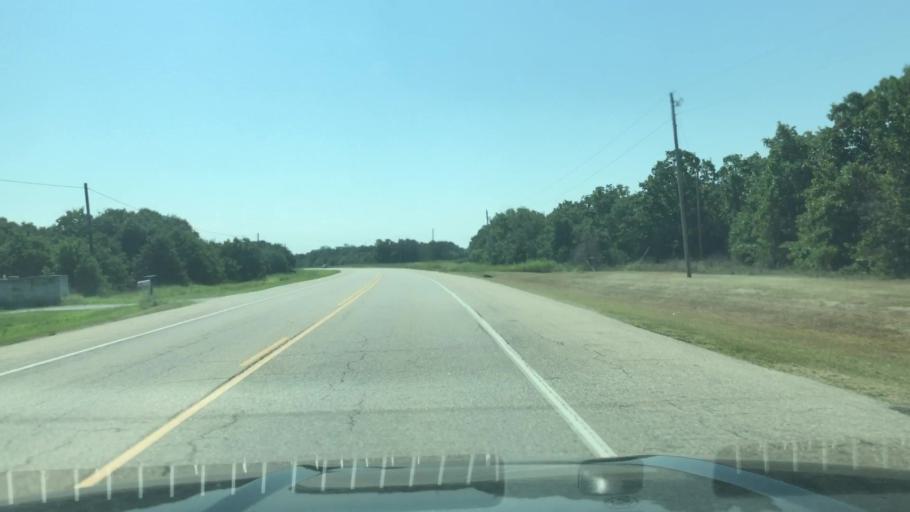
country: US
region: Oklahoma
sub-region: Creek County
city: Mannford
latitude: 35.9913
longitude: -96.3522
